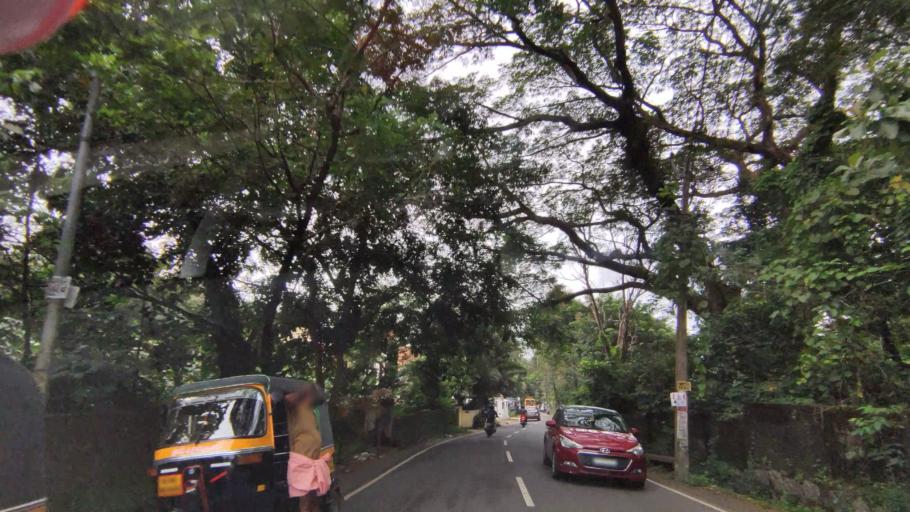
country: IN
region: Kerala
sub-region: Kottayam
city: Kottayam
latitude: 9.6318
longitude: 76.5147
